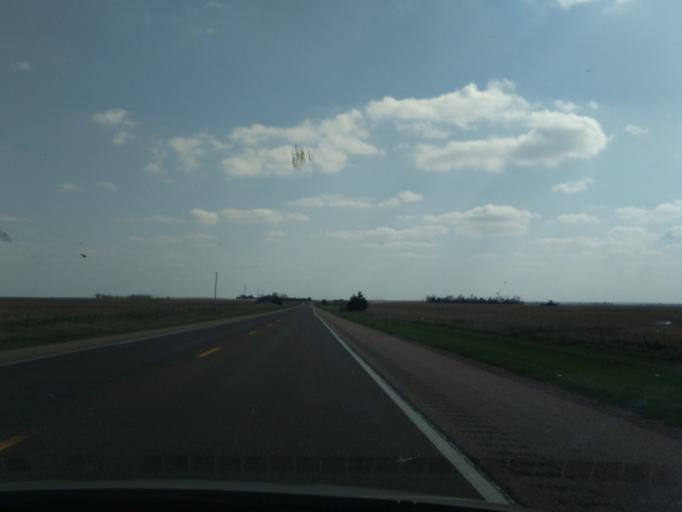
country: US
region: Nebraska
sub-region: Nuckolls County
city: Superior
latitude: 40.1025
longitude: -98.0671
